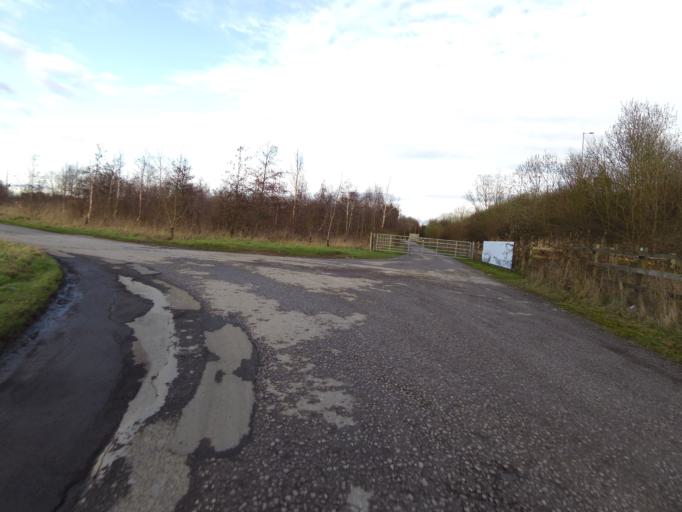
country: GB
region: England
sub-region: North Yorkshire
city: Brayton
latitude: 53.7641
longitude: -1.0759
